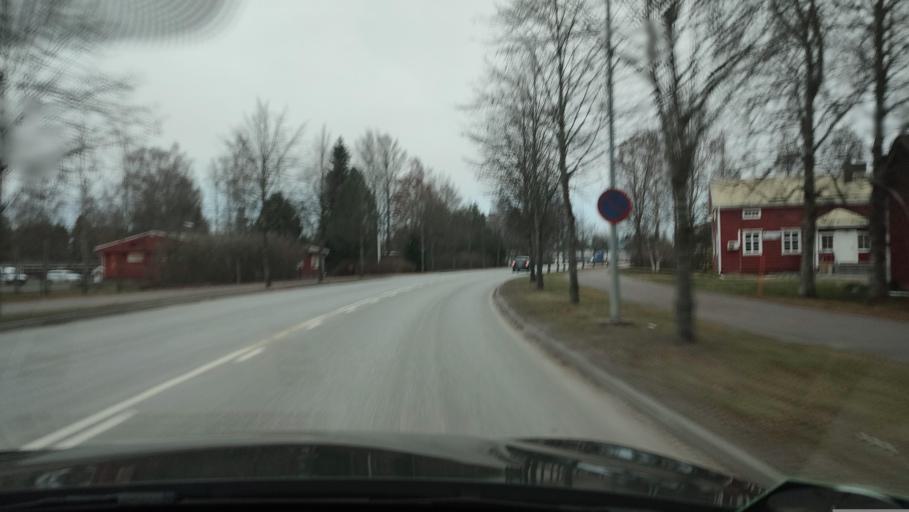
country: FI
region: Southern Ostrobothnia
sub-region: Suupohja
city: Kauhajoki
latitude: 62.4199
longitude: 22.1765
